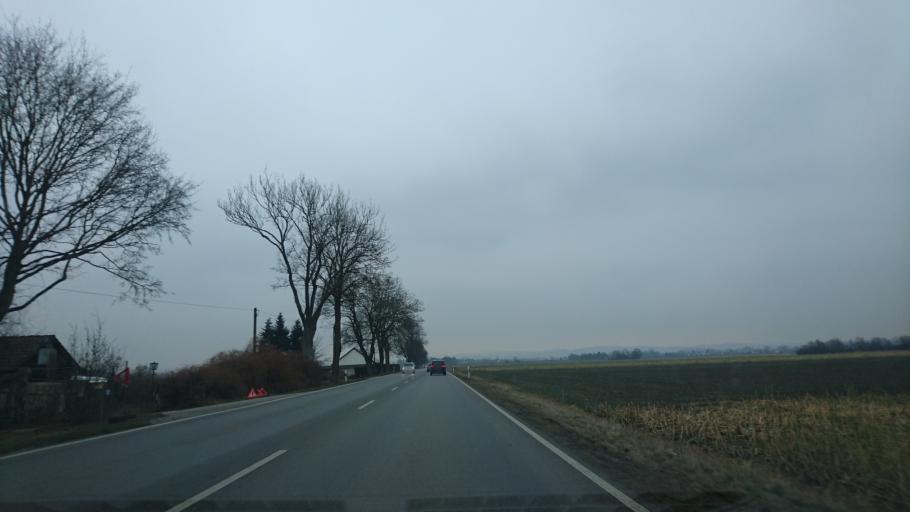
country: DE
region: Bavaria
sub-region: Lower Bavaria
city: Pocking
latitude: 48.4289
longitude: 13.3623
